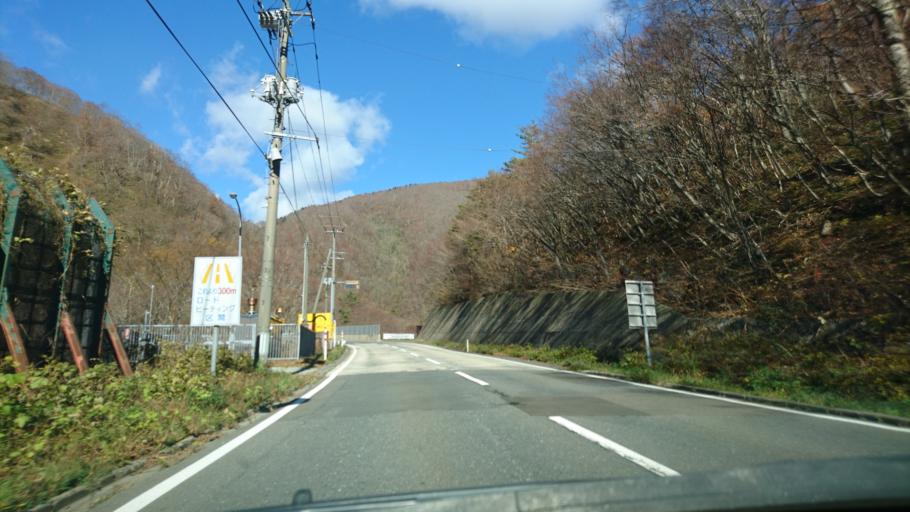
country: JP
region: Iwate
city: Kitakami
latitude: 39.3054
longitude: 140.8926
